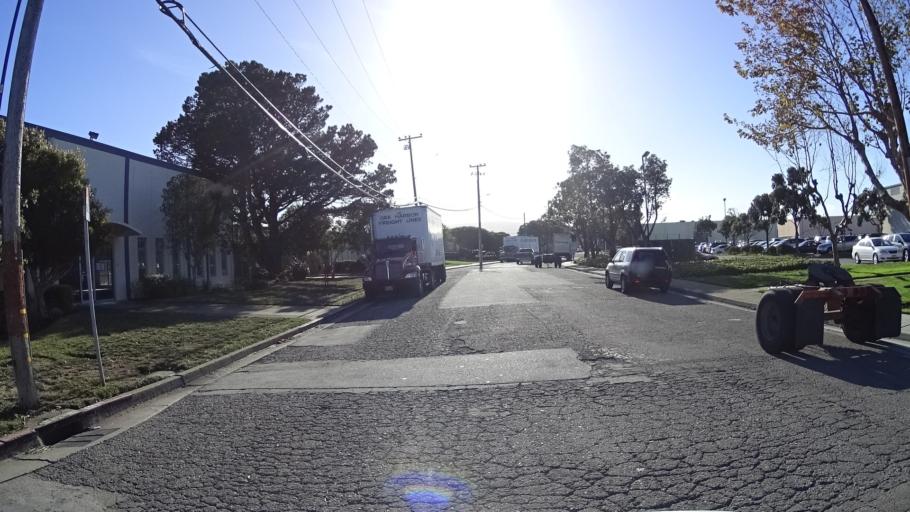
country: US
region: California
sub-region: San Mateo County
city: South San Francisco
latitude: 37.6448
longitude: -122.3962
